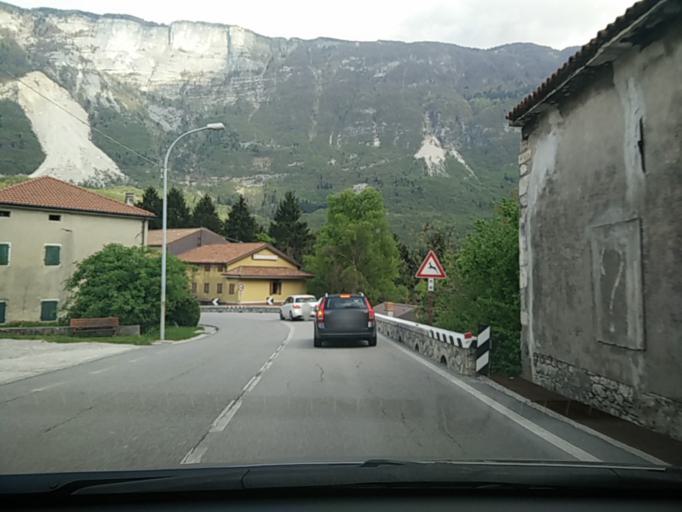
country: IT
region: Veneto
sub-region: Provincia di Belluno
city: Farra d'Alpago
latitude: 46.0779
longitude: 12.3345
